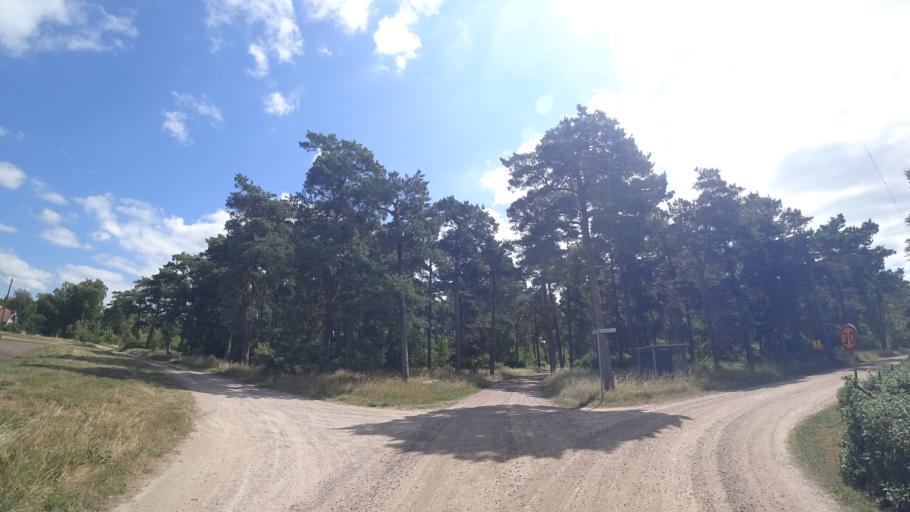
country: SE
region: Skane
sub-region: Kristianstads Kommun
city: Ahus
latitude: 55.9650
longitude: 14.2831
